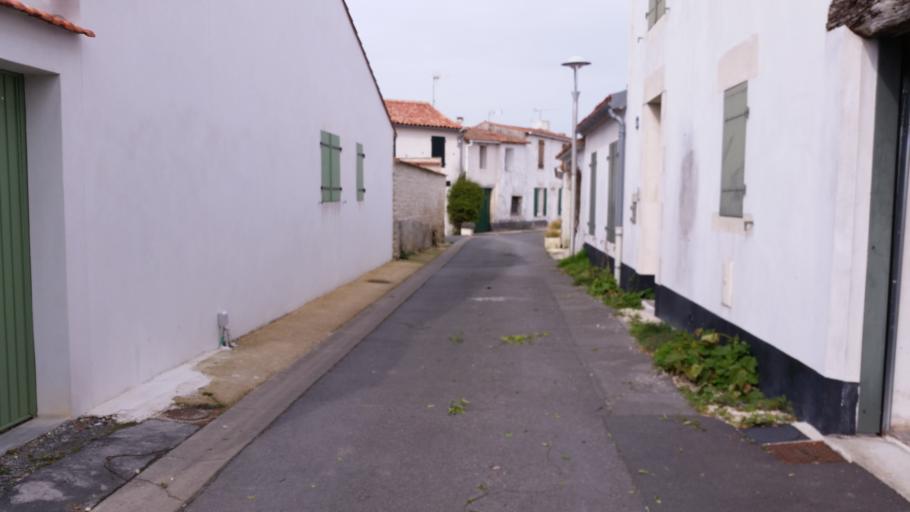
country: FR
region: Poitou-Charentes
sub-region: Departement de la Charente-Maritime
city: La Flotte
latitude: 46.1849
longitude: -1.3243
